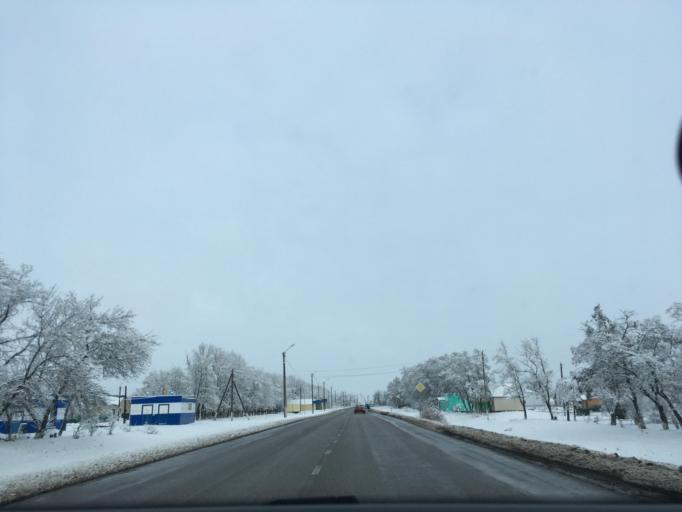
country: RU
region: Voronezj
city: Ol'khovatka
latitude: 50.0370
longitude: 39.0757
